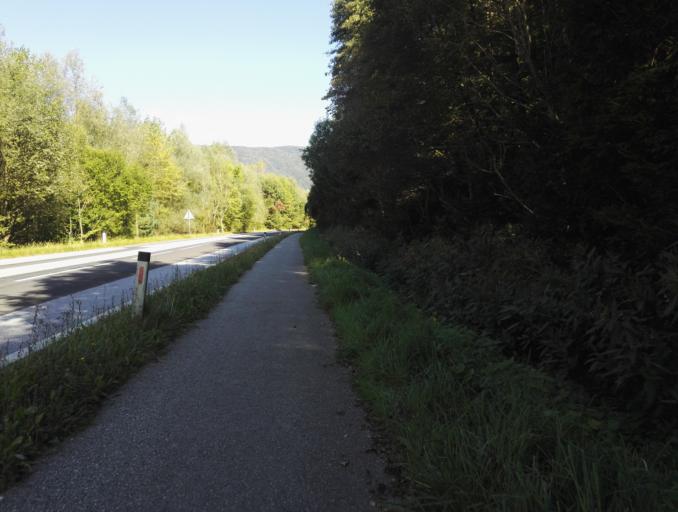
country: AT
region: Styria
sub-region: Politischer Bezirk Graz-Umgebung
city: Deutschfeistritz
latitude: 47.1871
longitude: 15.3390
